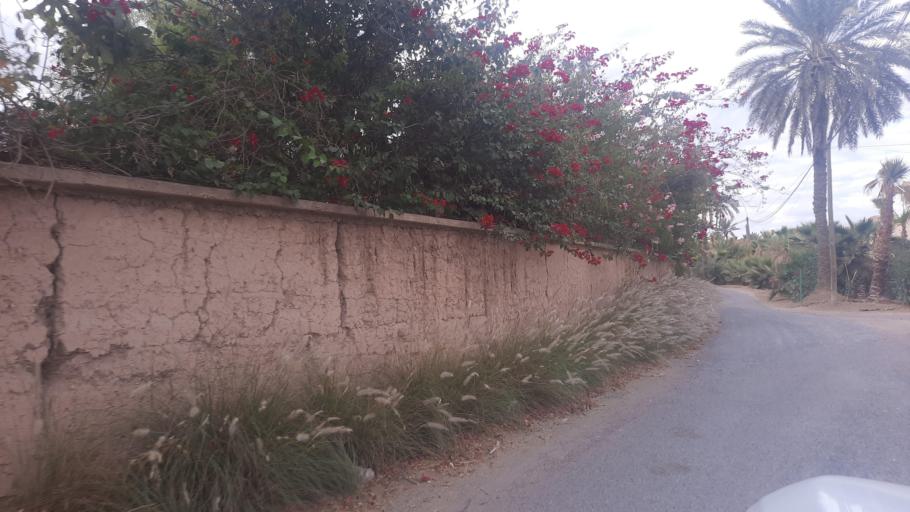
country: MA
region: Marrakech-Tensift-Al Haouz
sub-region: Marrakech
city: Marrakesh
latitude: 31.6756
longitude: -7.9531
